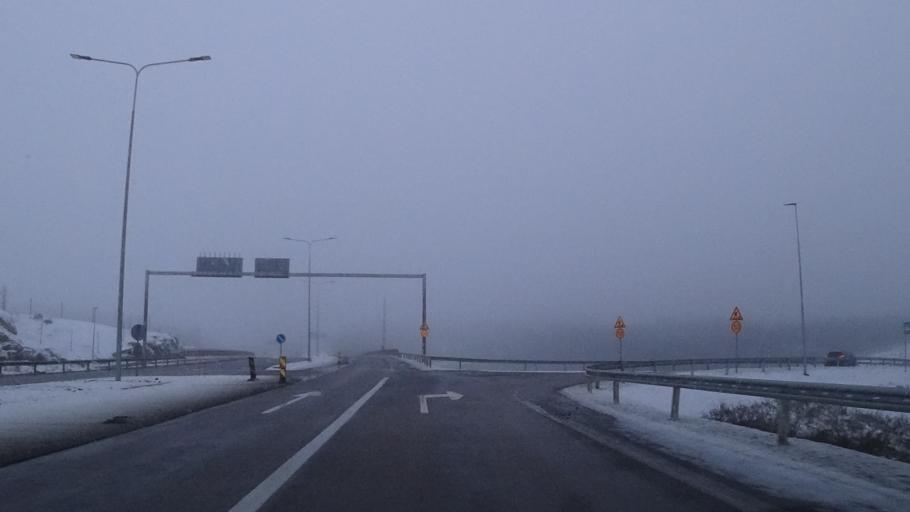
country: FI
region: Paijanne Tavastia
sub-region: Lahti
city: Hollola
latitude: 60.9813
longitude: 25.4865
